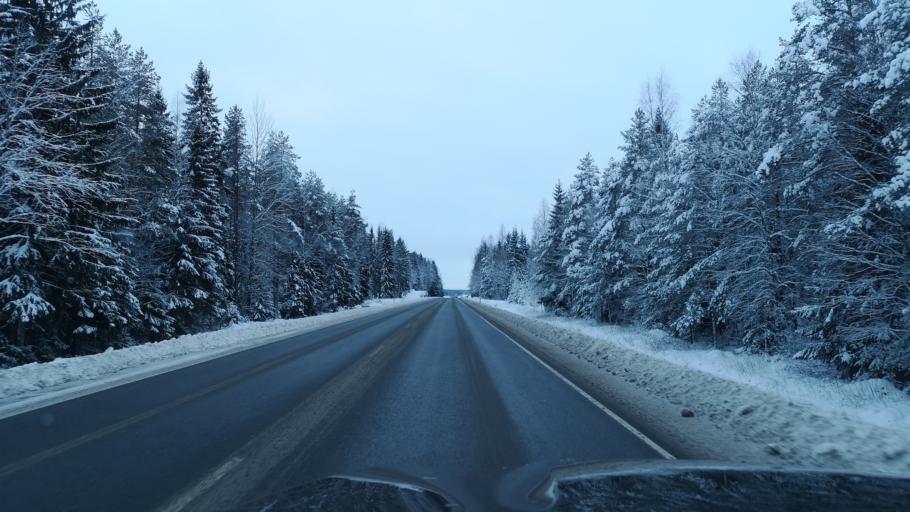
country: FI
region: Varsinais-Suomi
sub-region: Loimaa
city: Loimaa
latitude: 60.9011
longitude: 23.1392
